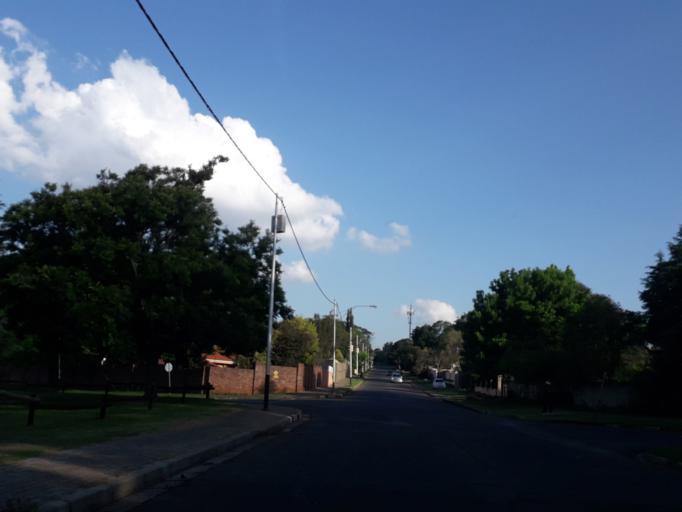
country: ZA
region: Gauteng
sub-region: City of Johannesburg Metropolitan Municipality
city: Johannesburg
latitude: -26.1499
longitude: 27.9948
